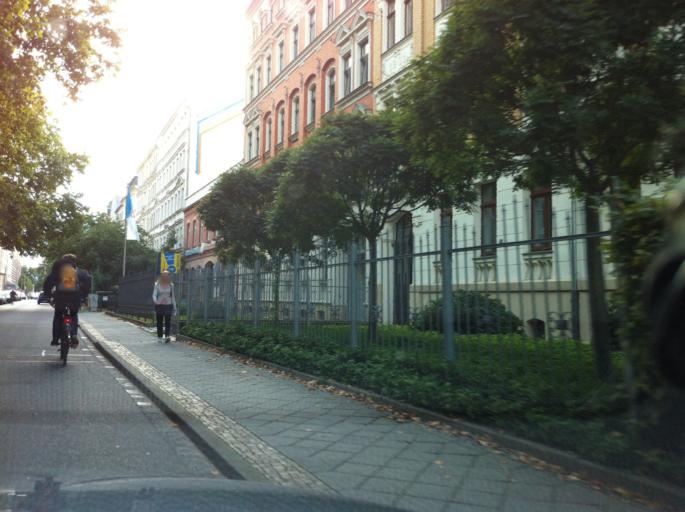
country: DE
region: Saxony
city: Leipzig
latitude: 51.3298
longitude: 12.3450
